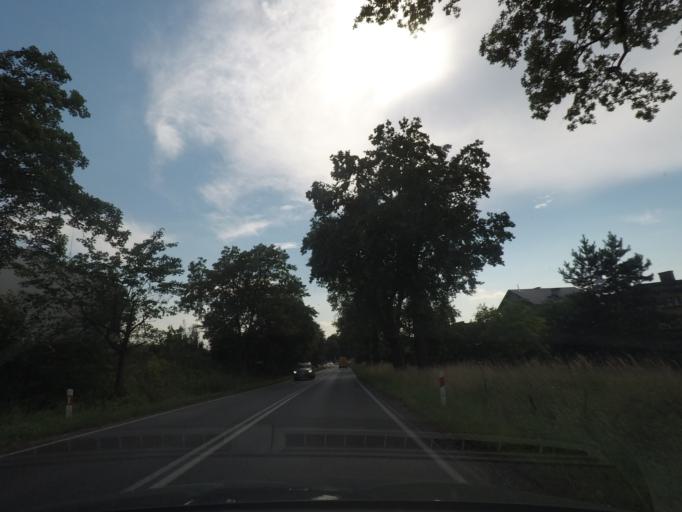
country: PL
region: Lesser Poland Voivodeship
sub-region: Powiat oswiecimski
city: Brzeszcze
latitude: 49.9809
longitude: 19.1524
